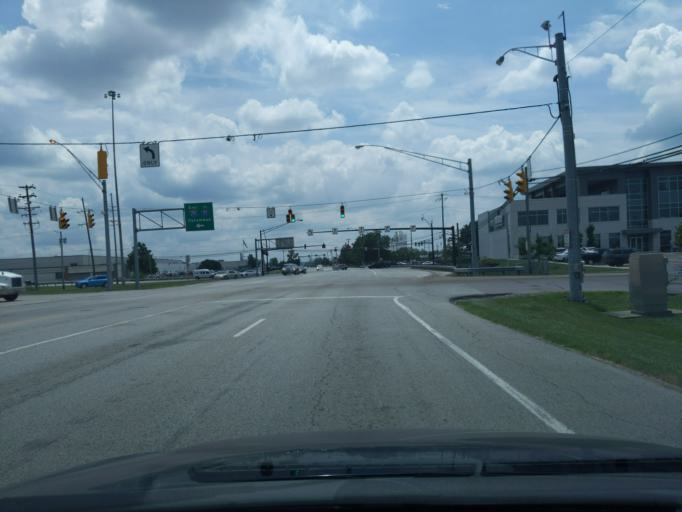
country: US
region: Ohio
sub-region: Hamilton County
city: Sharonville
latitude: 39.2856
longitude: -84.4294
